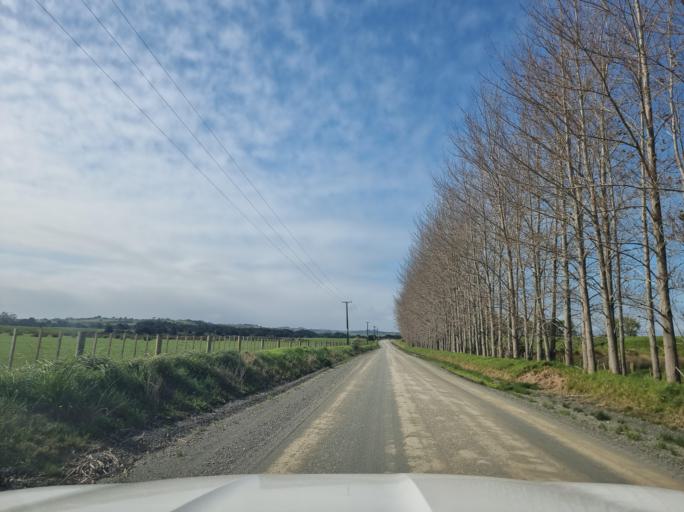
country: NZ
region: Auckland
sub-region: Auckland
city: Wellsford
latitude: -36.1171
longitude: 174.5014
